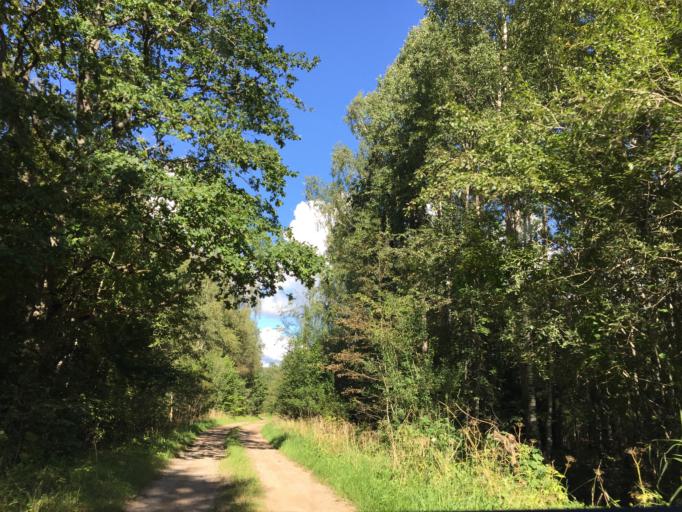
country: LV
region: Kuldigas Rajons
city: Kuldiga
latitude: 56.9768
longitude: 21.9084
